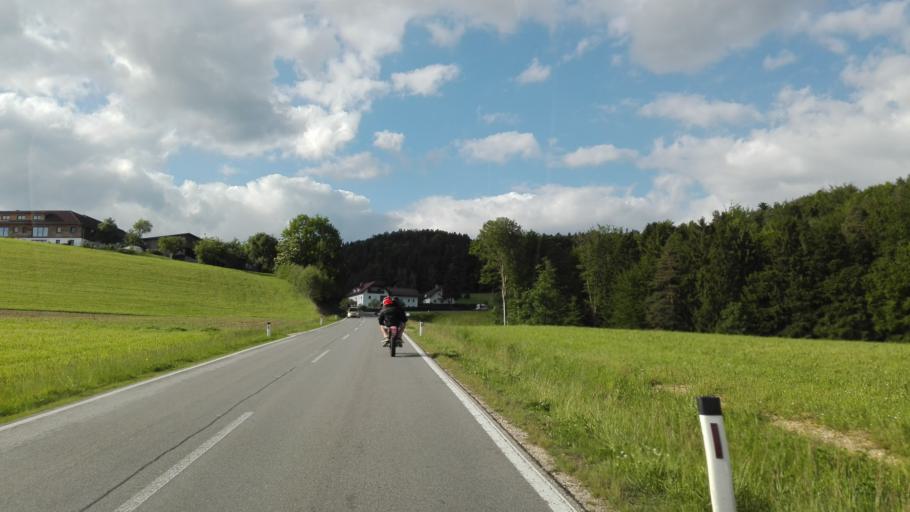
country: AT
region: Upper Austria
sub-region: Politischer Bezirk Perg
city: Perg
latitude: 48.3844
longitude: 14.7069
